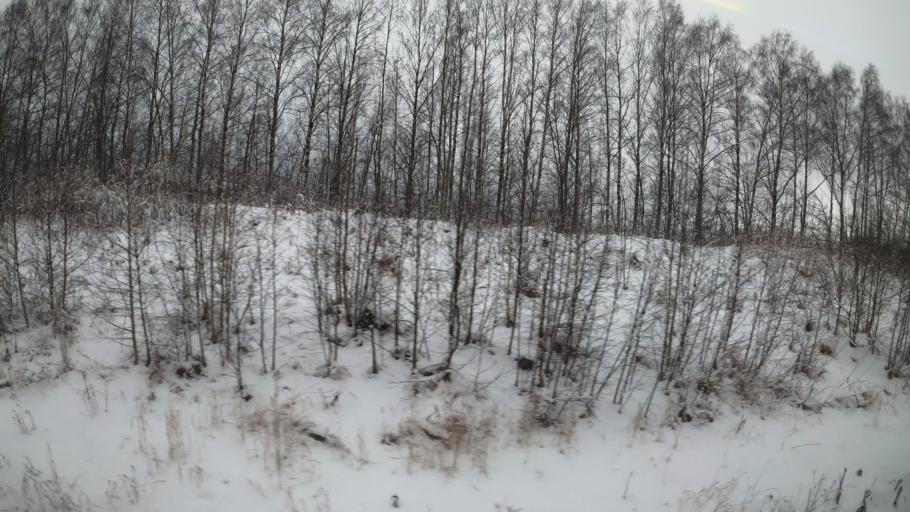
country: RU
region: Jaroslavl
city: Pereslavl'-Zalesskiy
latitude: 56.6871
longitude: 38.9191
